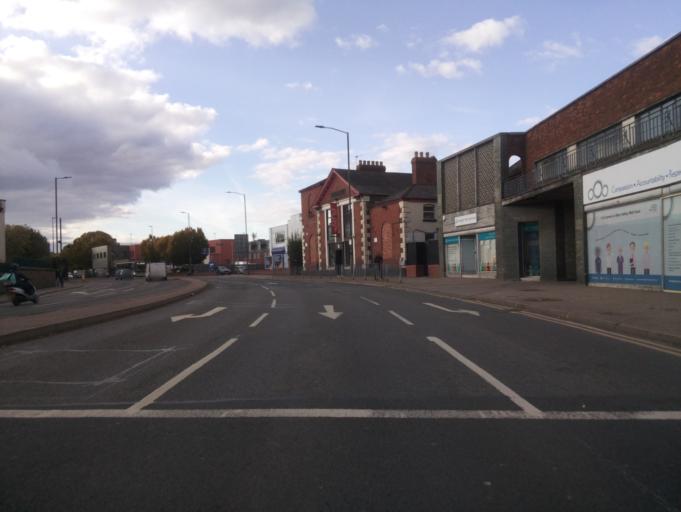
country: GB
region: England
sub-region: Herefordshire
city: Hereford
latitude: 52.0580
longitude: -2.7126
